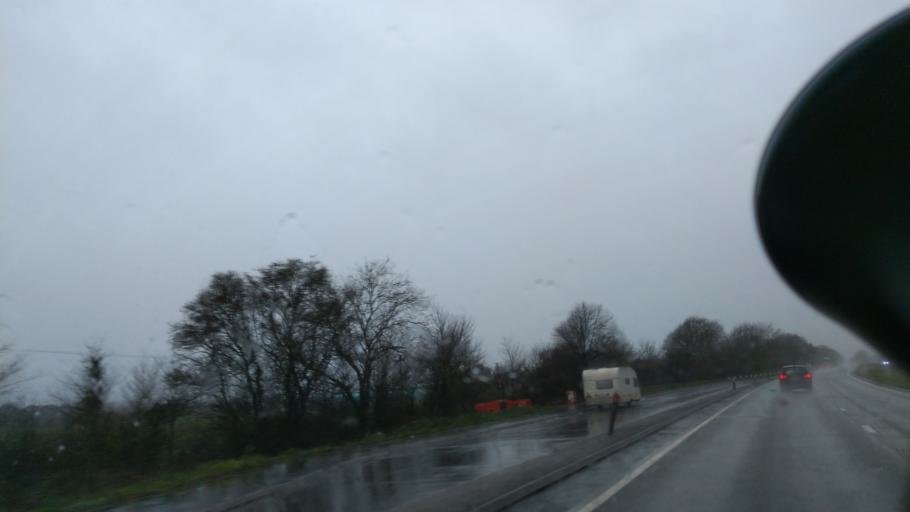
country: GB
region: England
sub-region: West Sussex
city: Rustington
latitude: 50.8410
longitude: -0.5005
